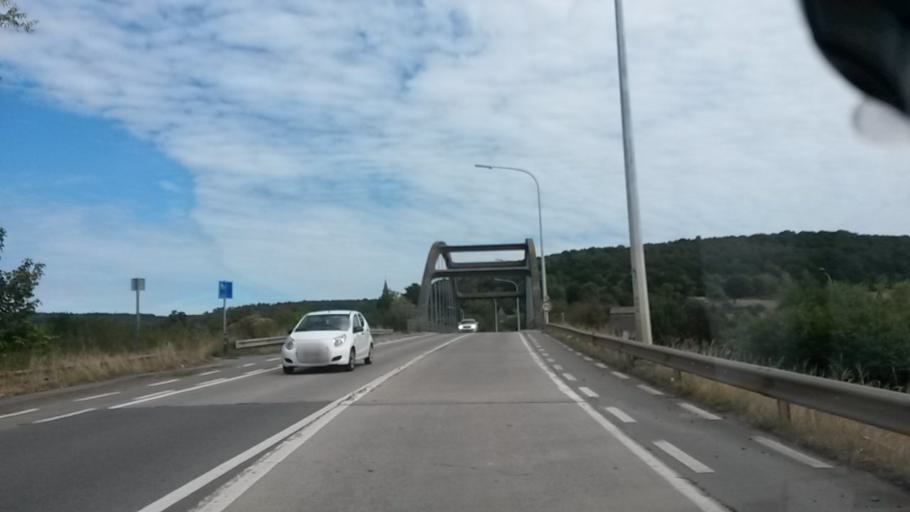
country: BE
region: Wallonia
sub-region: Province de Namur
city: Floreffe
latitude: 50.4484
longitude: 4.7680
